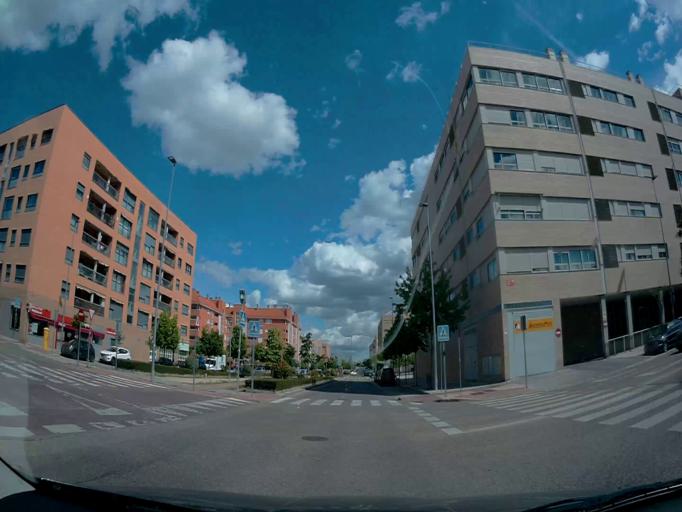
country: ES
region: Madrid
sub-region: Provincia de Madrid
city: San Sebastian de los Reyes
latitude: 40.5620
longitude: -3.6155
